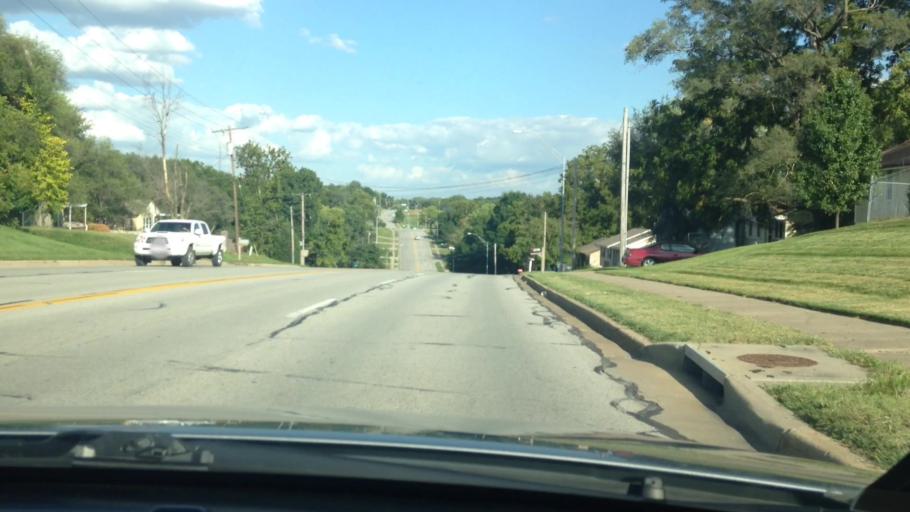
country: US
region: Missouri
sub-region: Clay County
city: Claycomo
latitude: 39.1807
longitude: -94.5206
